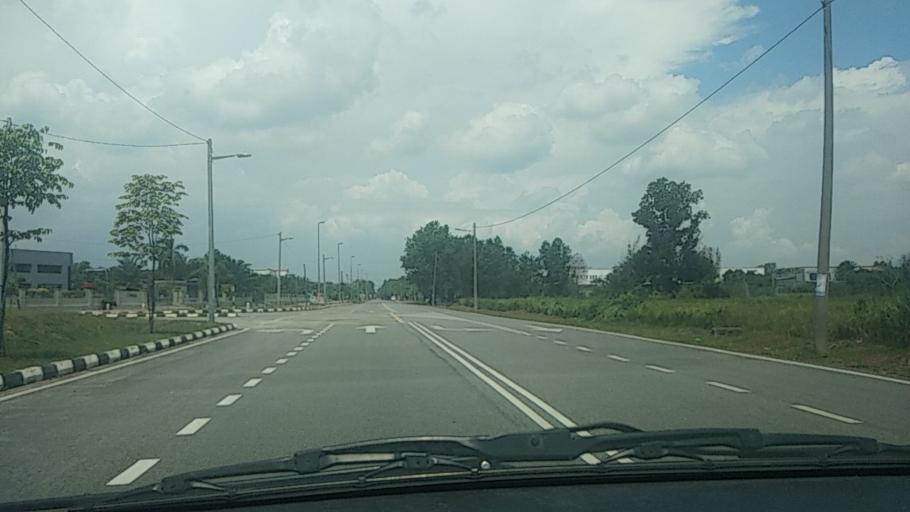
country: MY
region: Kedah
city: Sungai Petani
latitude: 5.6608
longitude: 100.5315
